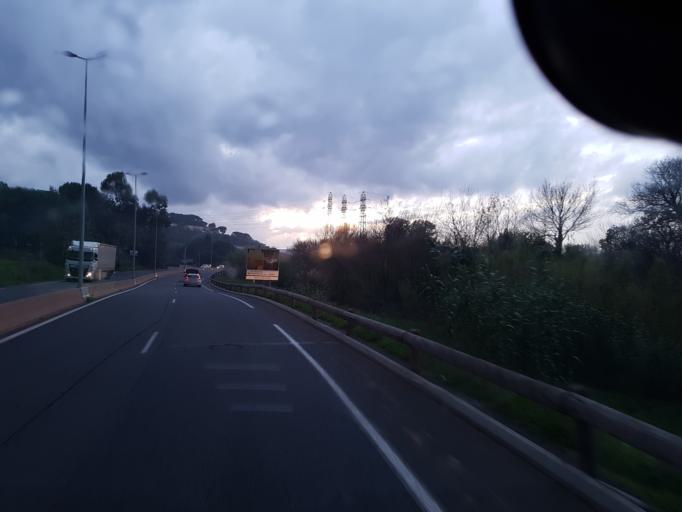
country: FR
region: Provence-Alpes-Cote d'Azur
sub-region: Departement du Var
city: Gassin
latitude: 43.2605
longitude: 6.5722
